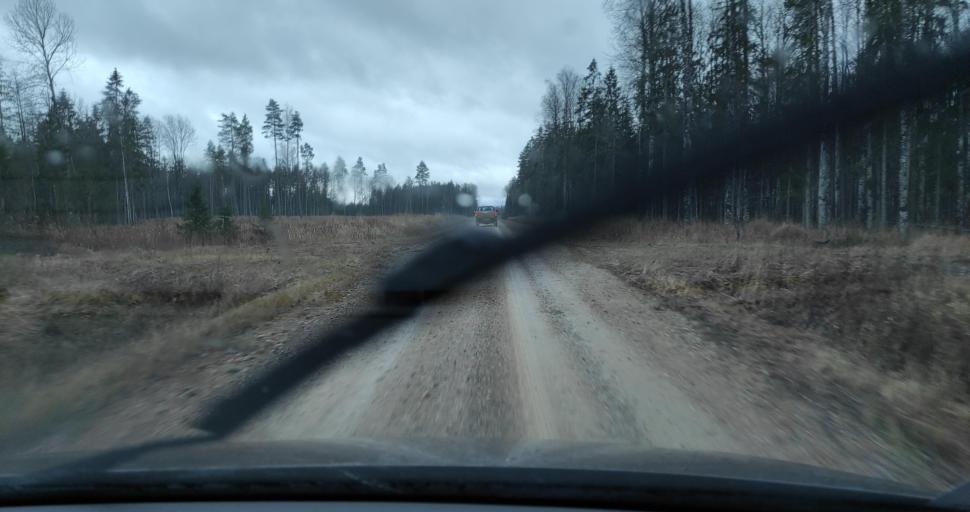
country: LV
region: Skrunda
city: Skrunda
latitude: 56.5609
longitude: 22.0798
